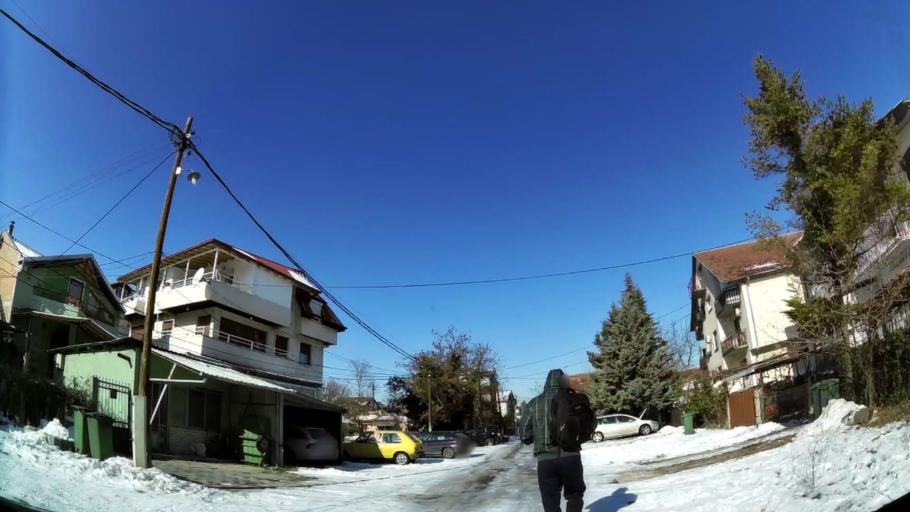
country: MK
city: Krushopek
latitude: 42.0046
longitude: 21.3598
